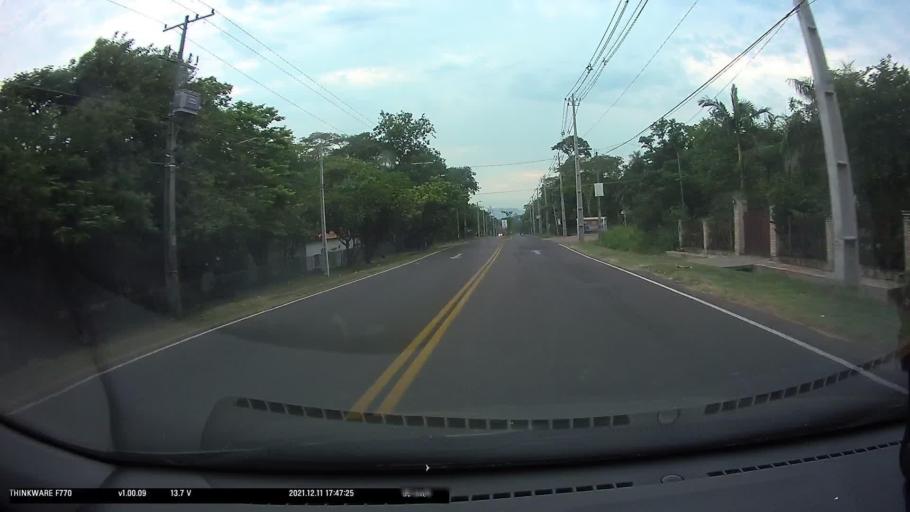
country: PY
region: Cordillera
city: San Bernardino
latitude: -25.2998
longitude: -57.2877
